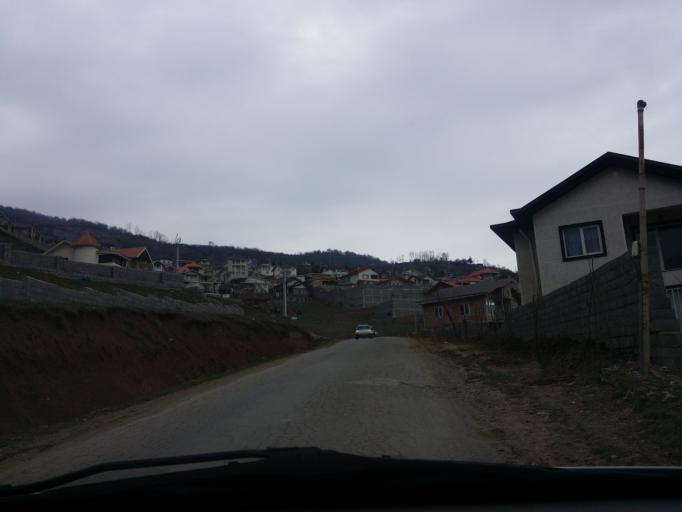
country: IR
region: Mazandaran
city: `Abbasabad
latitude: 36.5280
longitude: 51.1603
